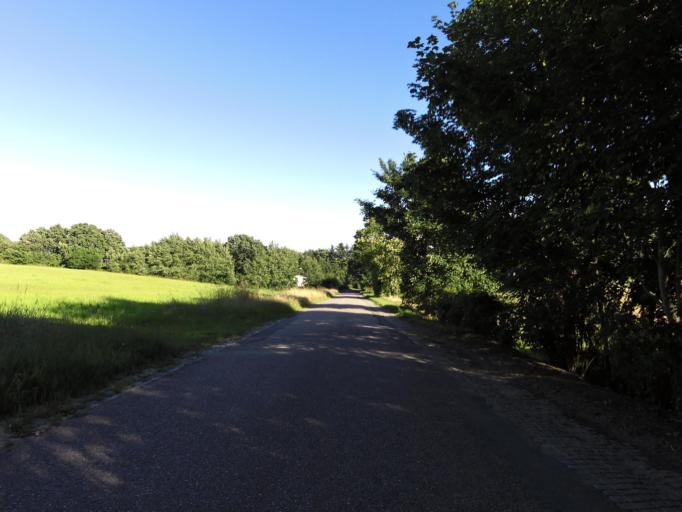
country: DK
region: South Denmark
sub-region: Haderslev Kommune
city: Gram
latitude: 55.3028
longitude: 9.1706
